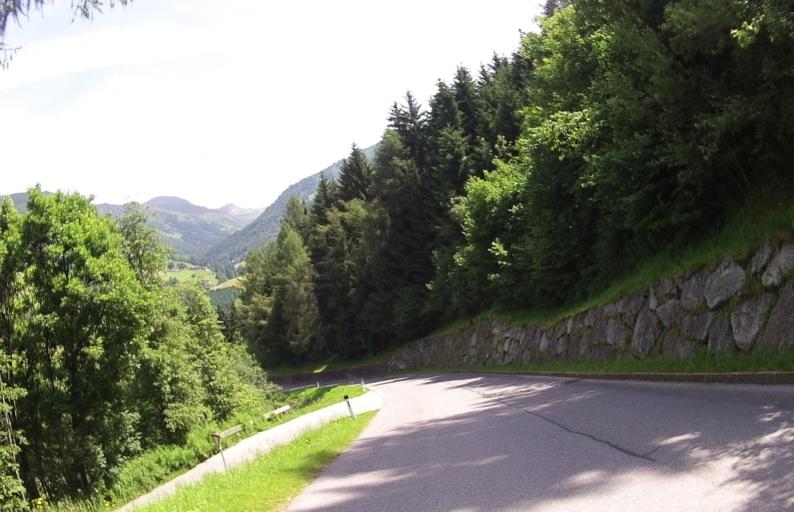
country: AT
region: Tyrol
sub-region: Politischer Bezirk Innsbruck Land
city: Ellbogen
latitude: 47.1600
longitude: 11.4528
